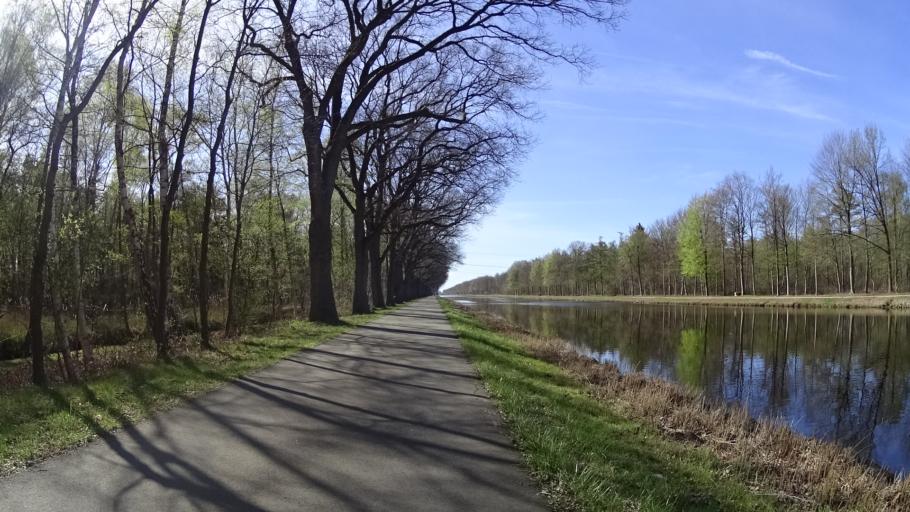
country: DE
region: Lower Saxony
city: Meppen
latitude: 52.6514
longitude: 7.3060
